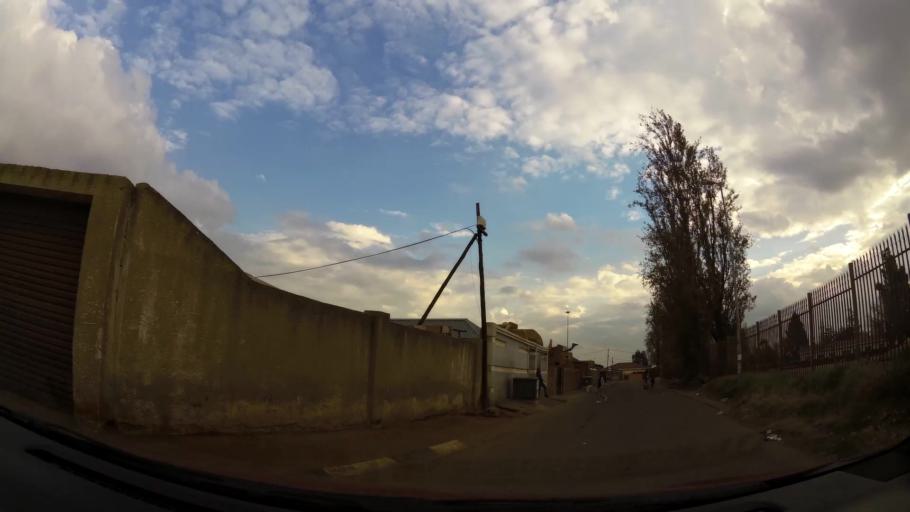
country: ZA
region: Gauteng
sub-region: City of Johannesburg Metropolitan Municipality
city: Soweto
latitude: -26.2417
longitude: 27.8259
